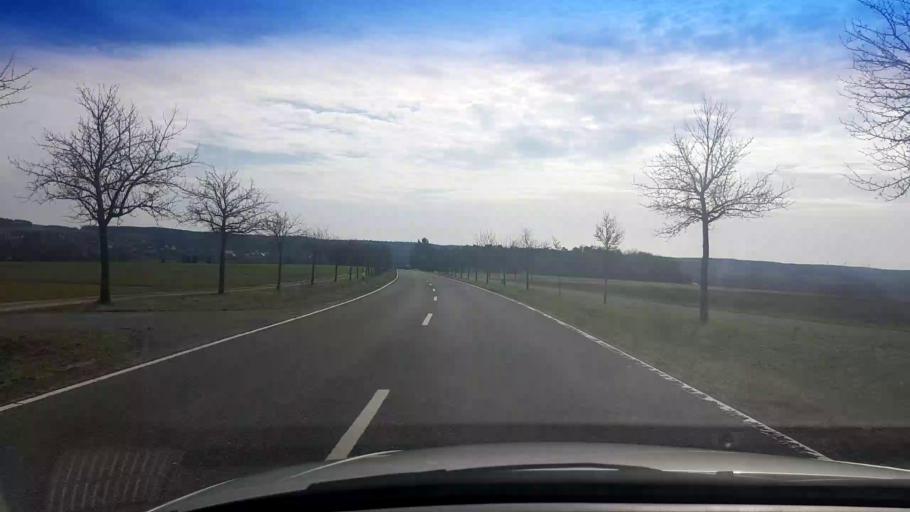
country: DE
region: Bavaria
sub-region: Upper Franconia
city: Frensdorf
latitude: 49.8315
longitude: 10.8692
